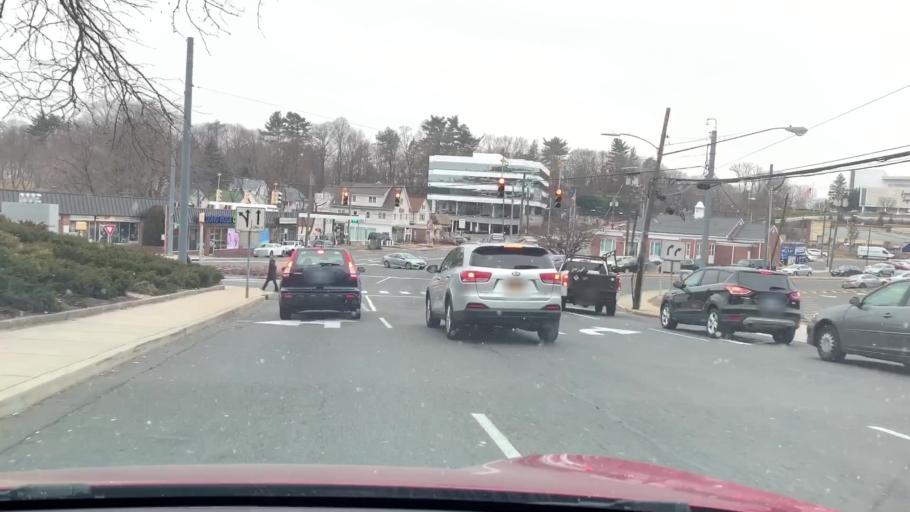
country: US
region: Connecticut
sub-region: Fairfield County
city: Stamford
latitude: 41.0714
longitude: -73.5486
